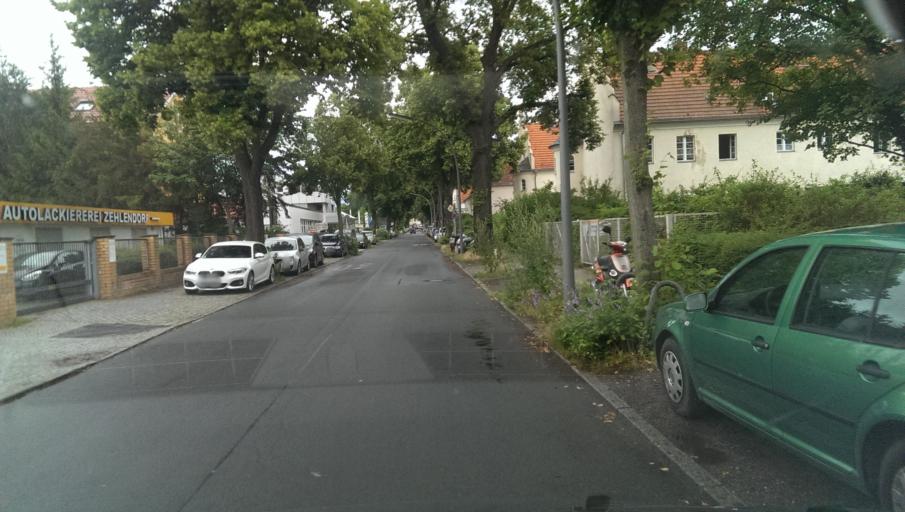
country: DE
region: Berlin
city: Zehlendorf Bezirk
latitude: 52.4281
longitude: 13.2518
